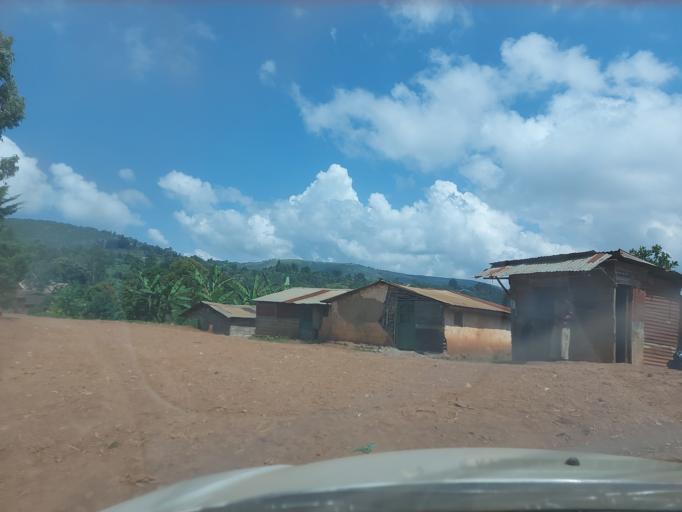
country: CD
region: South Kivu
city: Bukavu
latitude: -2.5068
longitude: 28.8338
